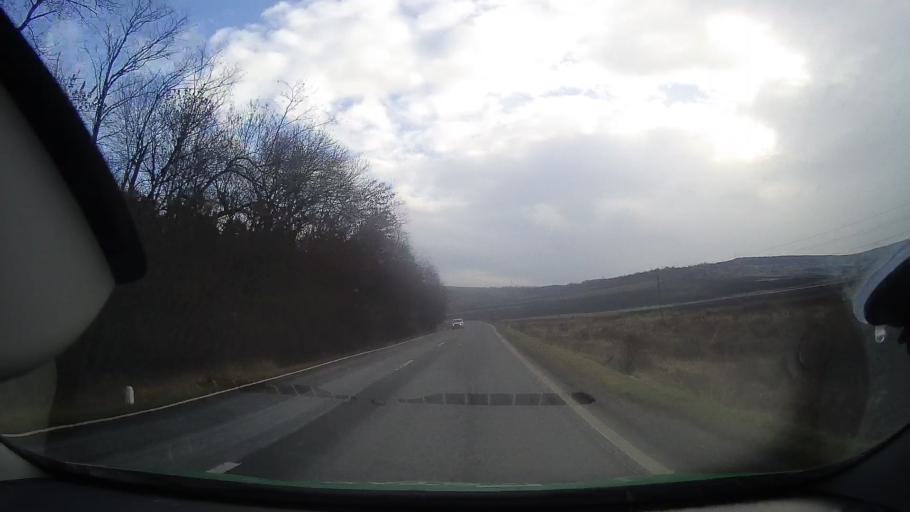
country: RO
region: Mures
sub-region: Comuna Cucerdea
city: Cucerdea
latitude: 46.3669
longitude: 24.2654
